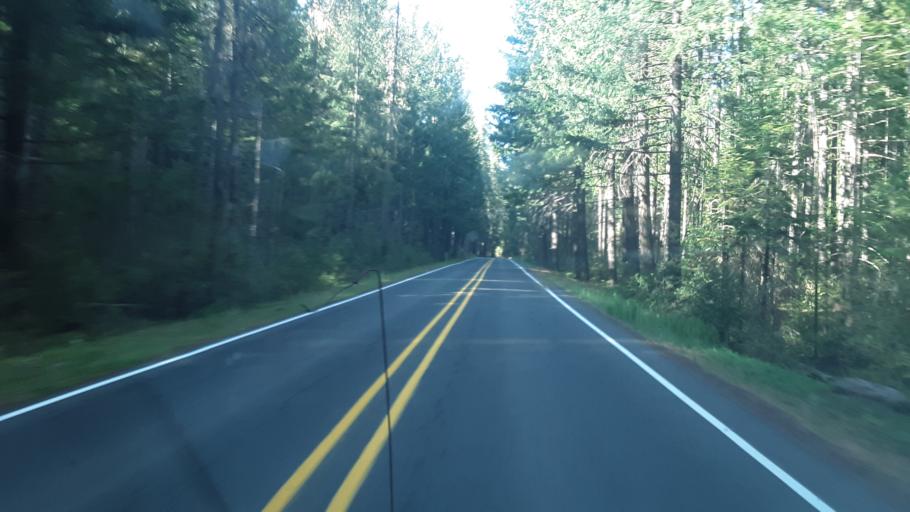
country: US
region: Oregon
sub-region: Jackson County
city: Shady Cove
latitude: 42.9313
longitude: -122.4223
